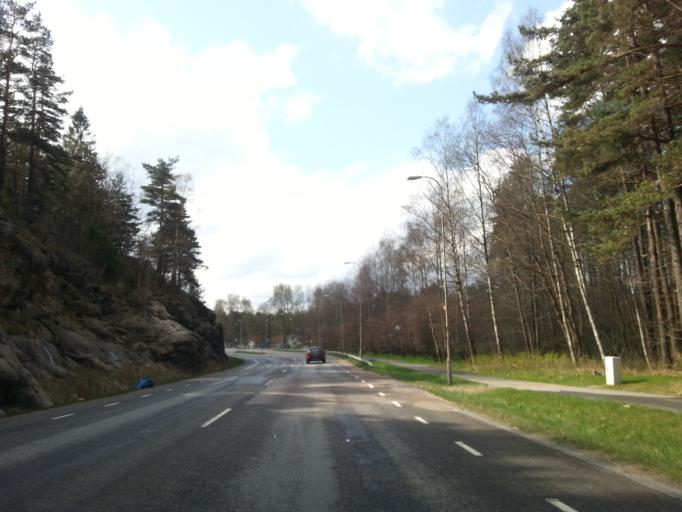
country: SE
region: Vaestra Goetaland
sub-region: Goteborg
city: Hammarkullen
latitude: 57.7783
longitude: 12.0224
